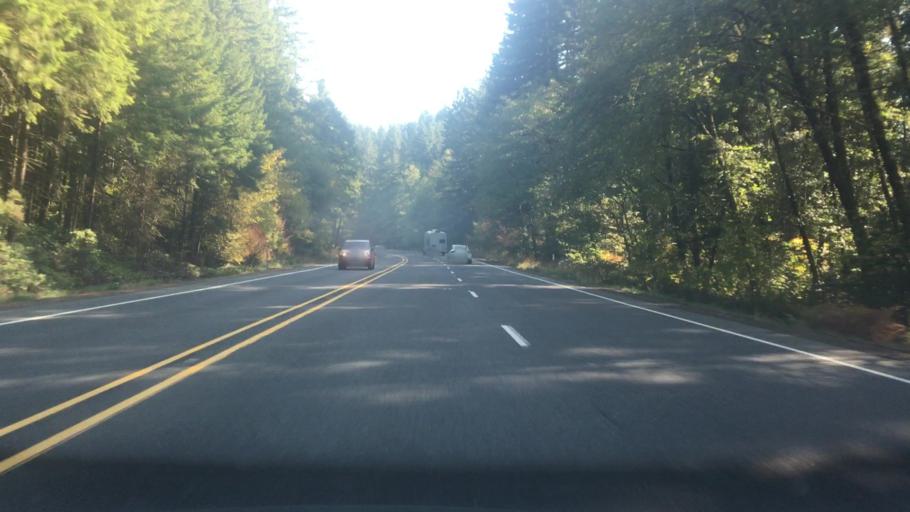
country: US
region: Oregon
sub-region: Polk County
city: Grand Ronde
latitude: 45.0624
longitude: -123.7028
